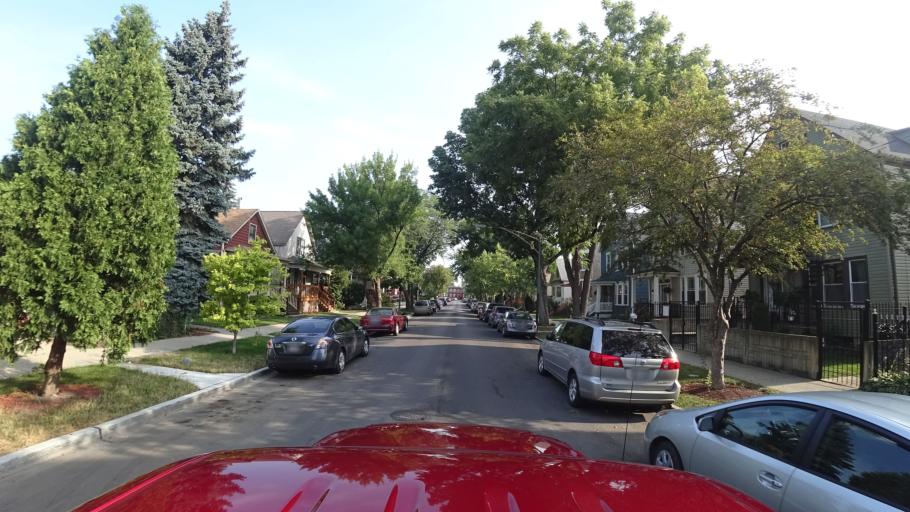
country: US
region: Illinois
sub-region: Cook County
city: Chicago
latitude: 41.8161
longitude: -87.6969
